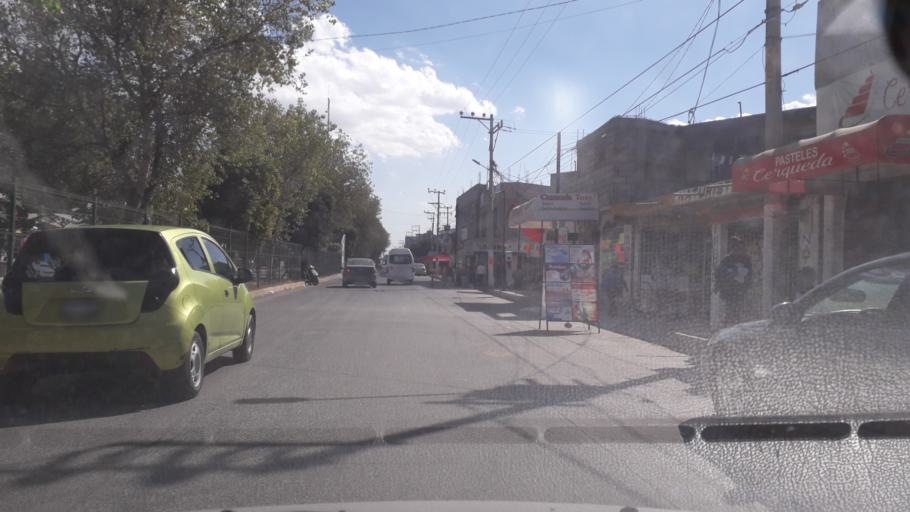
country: MX
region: Mexico
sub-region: Jaltenco
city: Alborada Jaltenco
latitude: 19.6505
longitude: -99.0645
